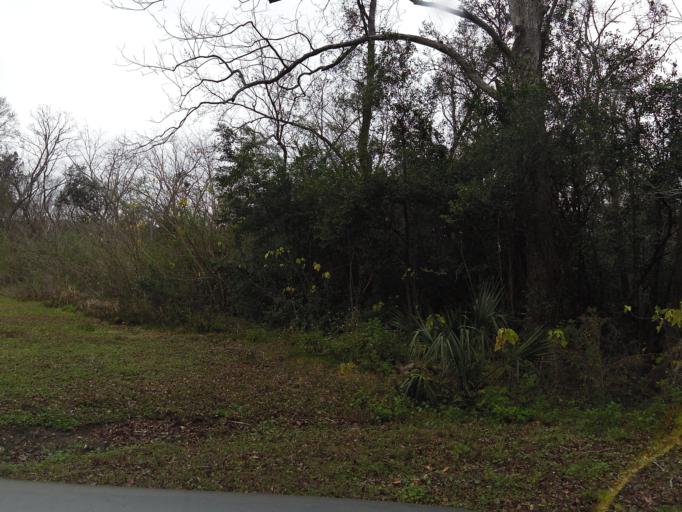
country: US
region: Florida
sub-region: Duval County
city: Jacksonville
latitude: 30.3766
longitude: -81.7227
